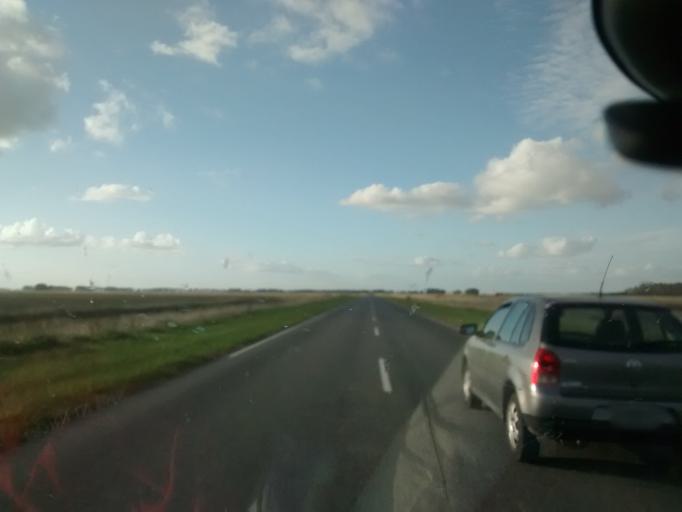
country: AR
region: Buenos Aires
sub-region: Partido de General Belgrano
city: General Belgrano
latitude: -36.1855
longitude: -58.5933
